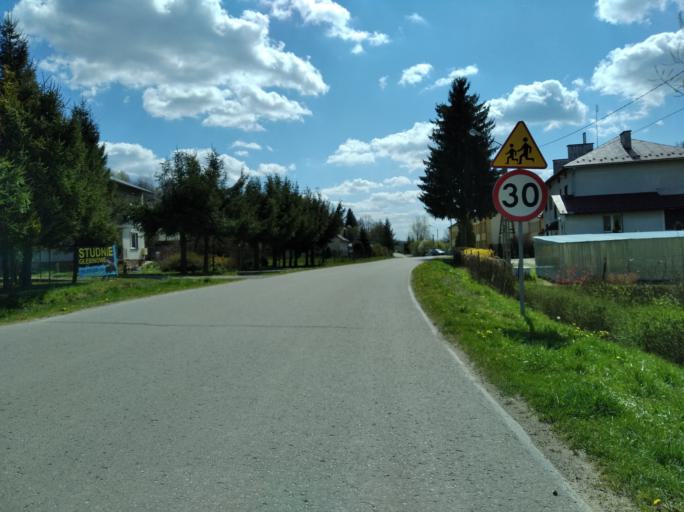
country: PL
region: Subcarpathian Voivodeship
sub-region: Powiat brzozowski
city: Wesola
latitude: 49.8051
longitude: 22.0896
